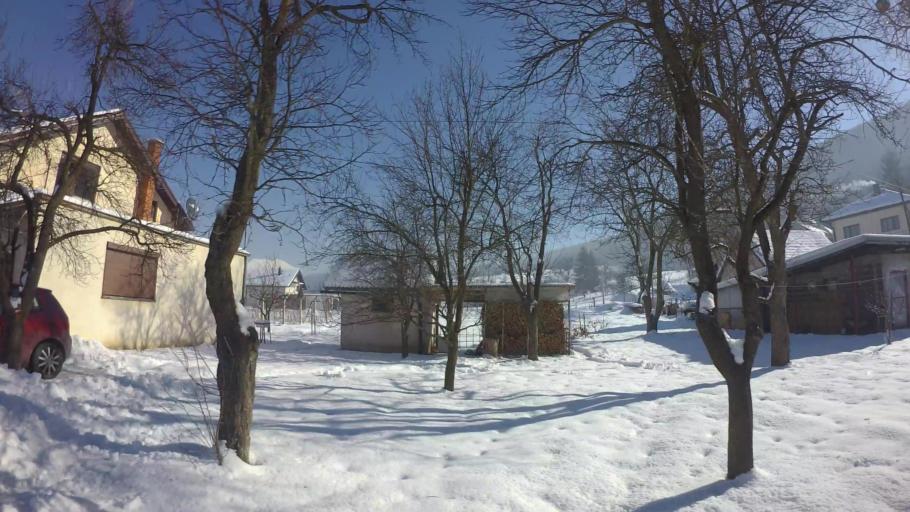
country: BA
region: Federation of Bosnia and Herzegovina
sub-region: Kanton Sarajevo
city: Sarajevo
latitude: 43.7886
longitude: 18.3408
